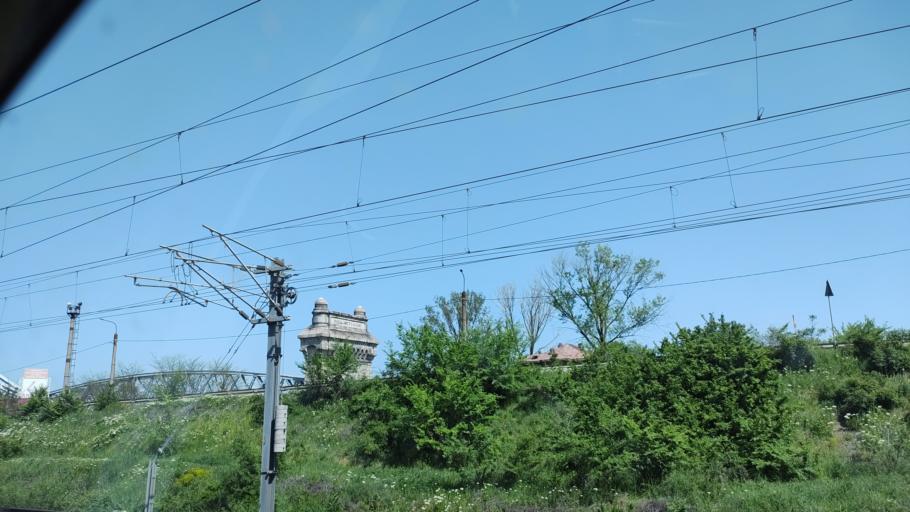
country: RO
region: Constanta
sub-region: Oras Cernavoda
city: Cernavoda
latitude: 44.3394
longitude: 28.0199
